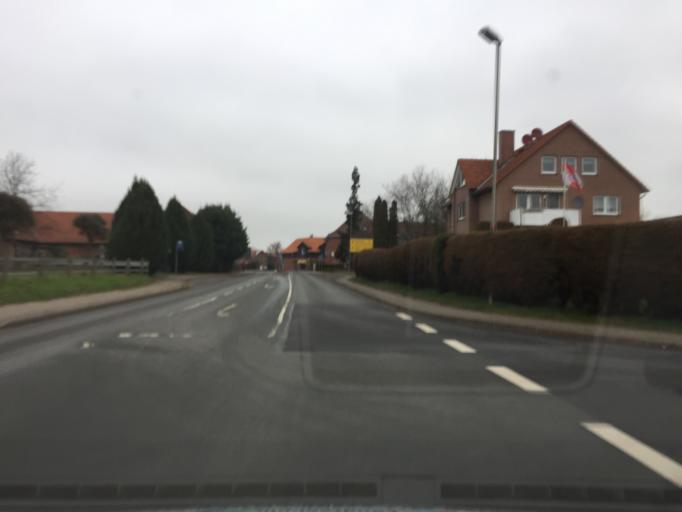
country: DE
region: Lower Saxony
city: Meerbeck
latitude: 52.3412
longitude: 9.1456
